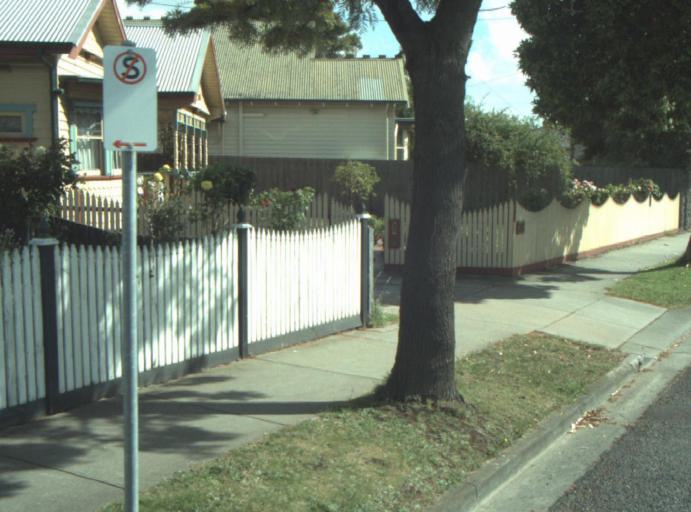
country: AU
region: Victoria
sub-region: Greater Geelong
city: Breakwater
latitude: -38.1789
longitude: 144.3385
